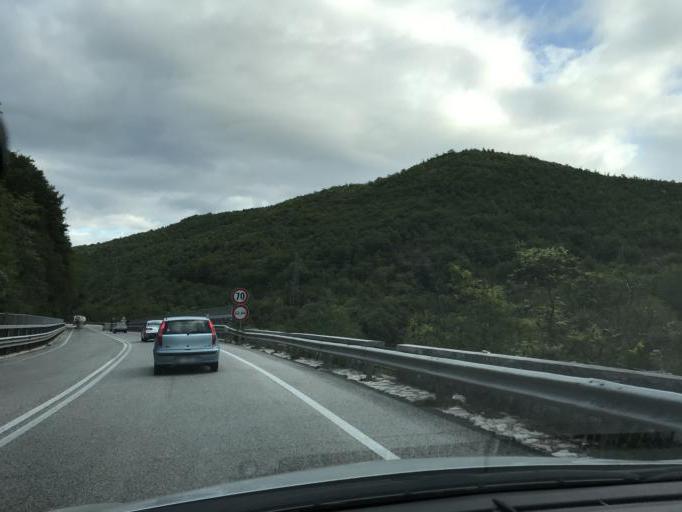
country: IT
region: Umbria
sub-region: Provincia di Perugia
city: Spoleto
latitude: 42.6811
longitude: 12.7269
